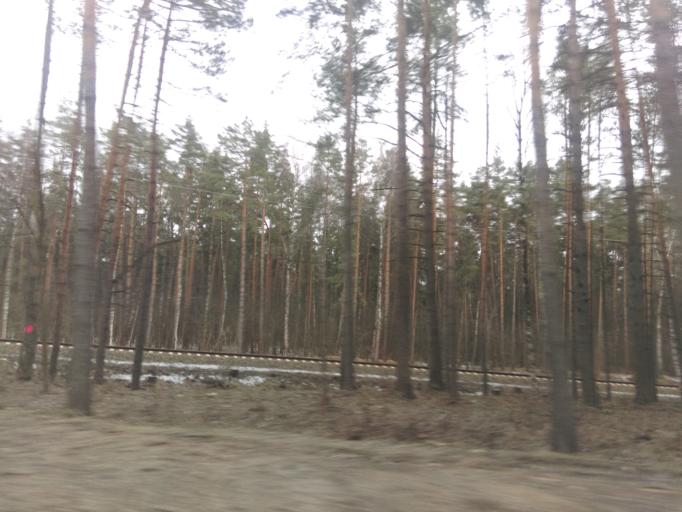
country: RU
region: Moskovskaya
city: Nemchinovka
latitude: 55.7500
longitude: 37.3259
